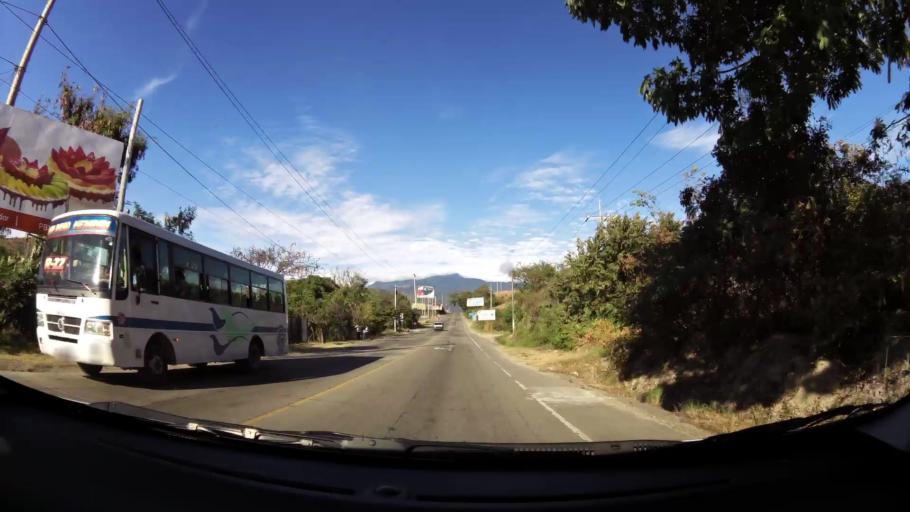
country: SV
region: Santa Ana
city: Metapan
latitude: 14.3127
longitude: -89.4501
